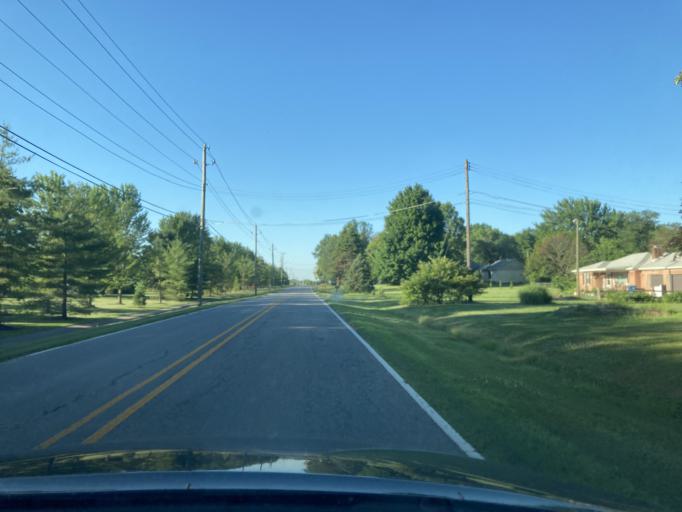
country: US
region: Indiana
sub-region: Marion County
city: Meridian Hills
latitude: 39.8798
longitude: -86.2221
